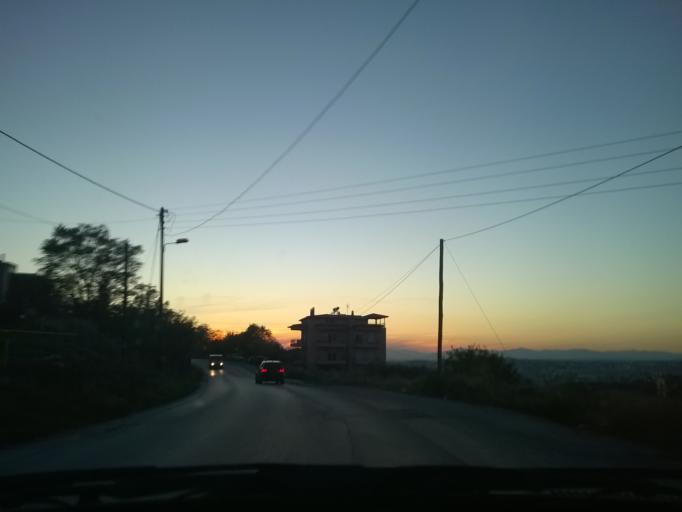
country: GR
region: Central Macedonia
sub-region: Nomos Thessalonikis
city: Polichni
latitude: 40.6665
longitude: 22.9586
